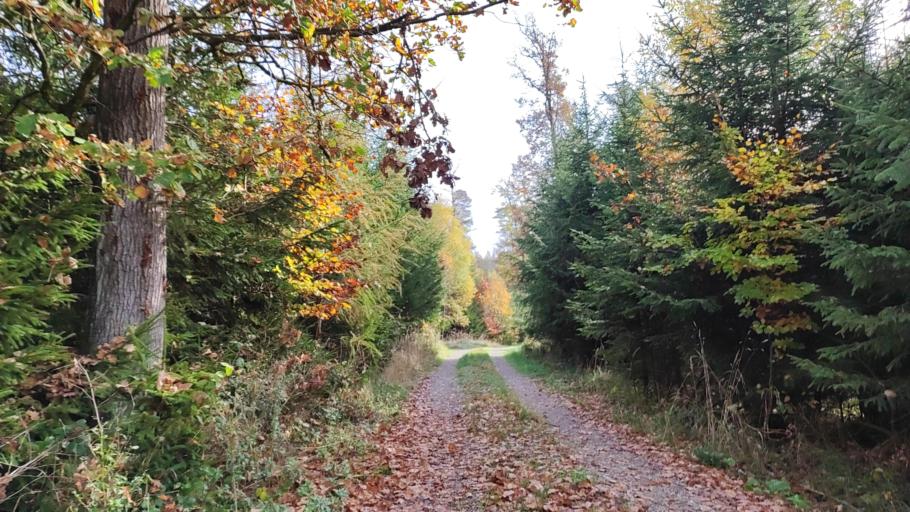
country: DE
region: Bavaria
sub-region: Swabia
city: Langenneufnach
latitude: 48.2947
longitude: 10.5924
